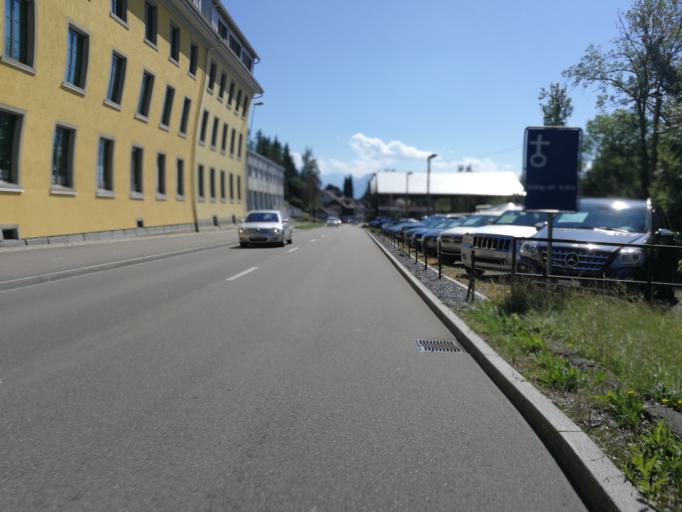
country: CH
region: Zurich
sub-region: Bezirk Hinwil
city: Durnten
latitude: 47.2816
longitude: 8.8430
